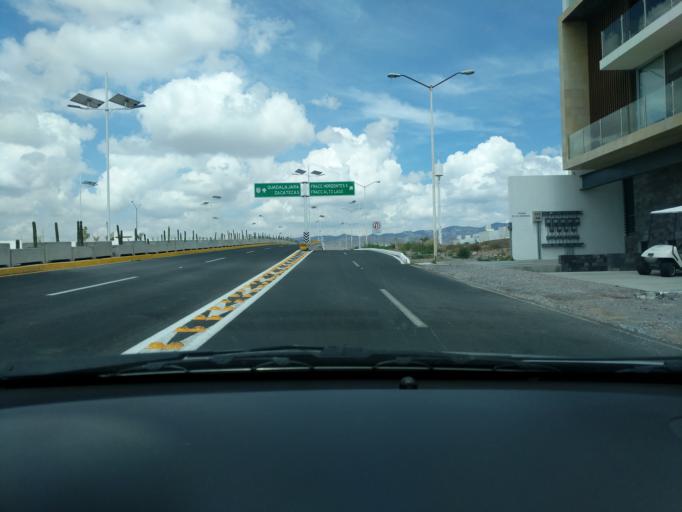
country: MX
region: San Luis Potosi
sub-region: Mexquitic de Carmona
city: Guadalupe Victoria
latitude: 22.1682
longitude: -101.0456
